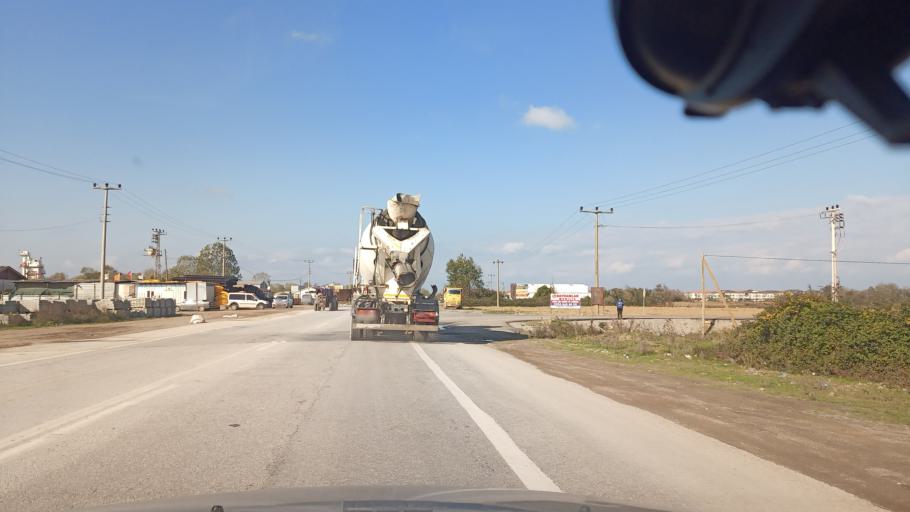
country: TR
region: Sakarya
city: Karasu
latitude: 41.1129
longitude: 30.6593
